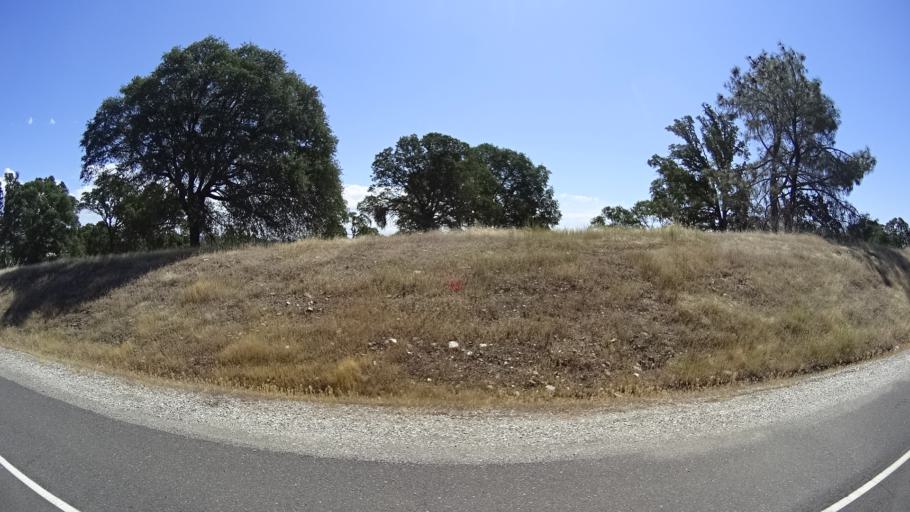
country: US
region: California
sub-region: Calaveras County
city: Copperopolis
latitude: 37.9574
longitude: -120.6519
